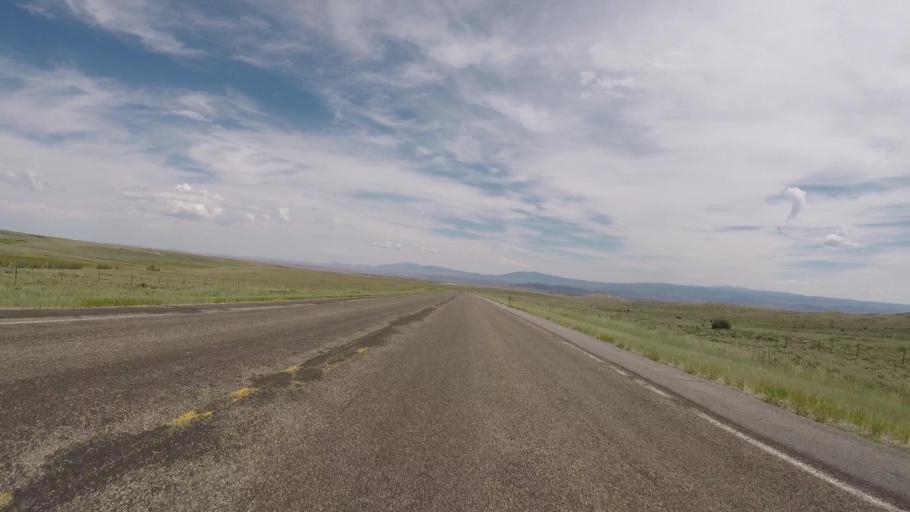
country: US
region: Wyoming
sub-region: Carbon County
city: Saratoga
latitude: 41.1915
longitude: -106.8516
